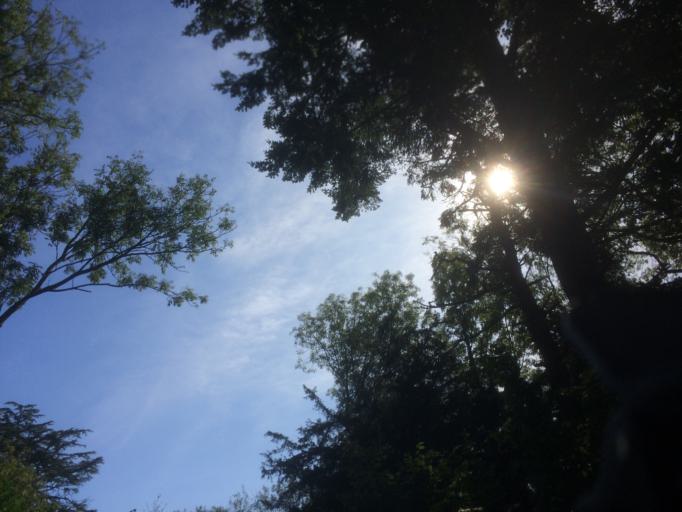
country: GB
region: England
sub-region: Devon
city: Horrabridge
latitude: 50.5197
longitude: -4.1252
